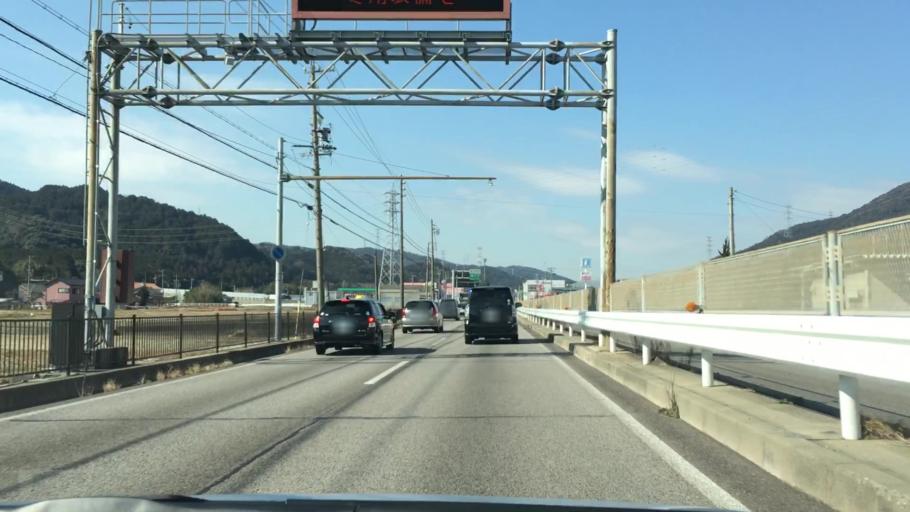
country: JP
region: Aichi
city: Gamagori
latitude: 34.8659
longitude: 137.2987
